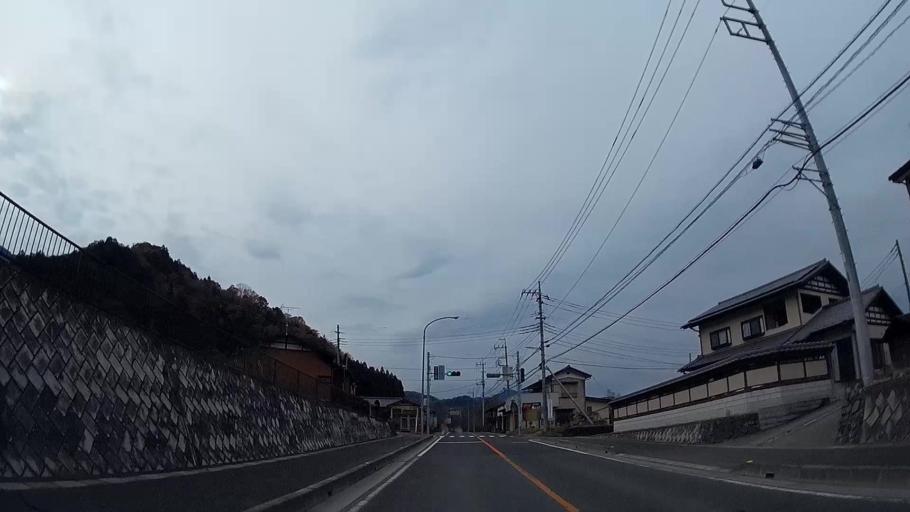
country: JP
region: Saitama
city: Chichibu
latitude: 35.9541
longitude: 139.0256
